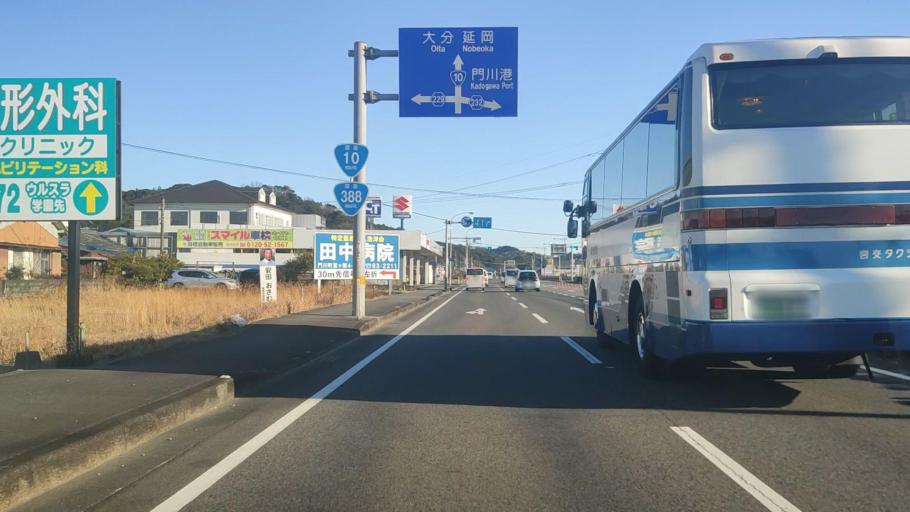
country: JP
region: Miyazaki
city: Nobeoka
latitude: 32.4785
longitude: 131.6555
